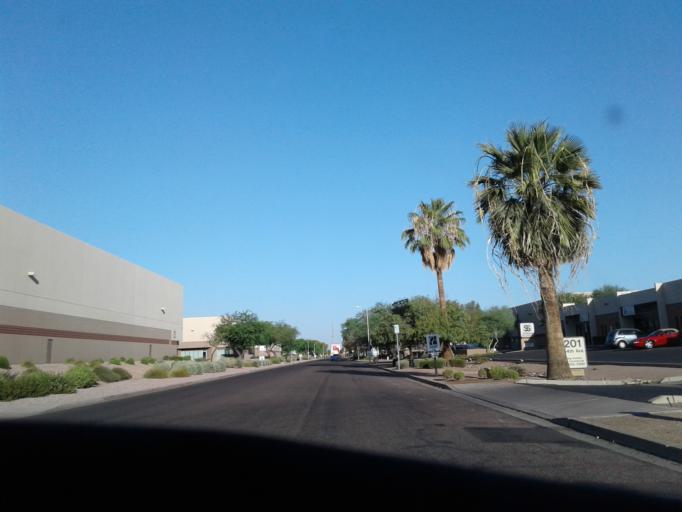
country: US
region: Arizona
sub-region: Maricopa County
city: Glendale
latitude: 33.4605
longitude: -112.1739
